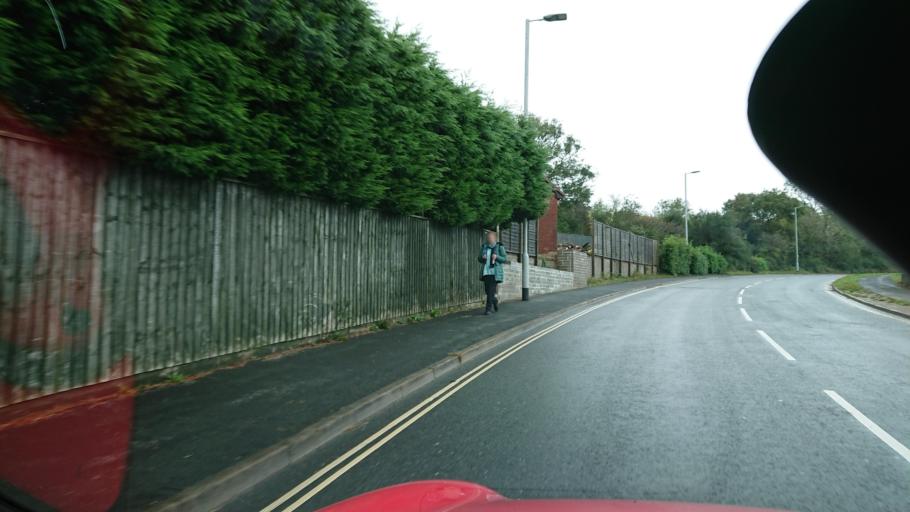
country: GB
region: England
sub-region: Devon
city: Plympton
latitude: 50.4200
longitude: -4.1050
